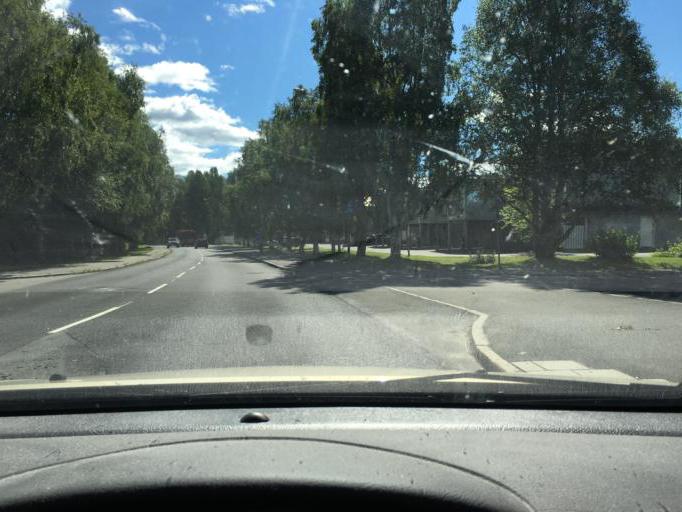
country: SE
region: Norrbotten
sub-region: Lulea Kommun
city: Lulea
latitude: 65.5961
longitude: 22.1367
